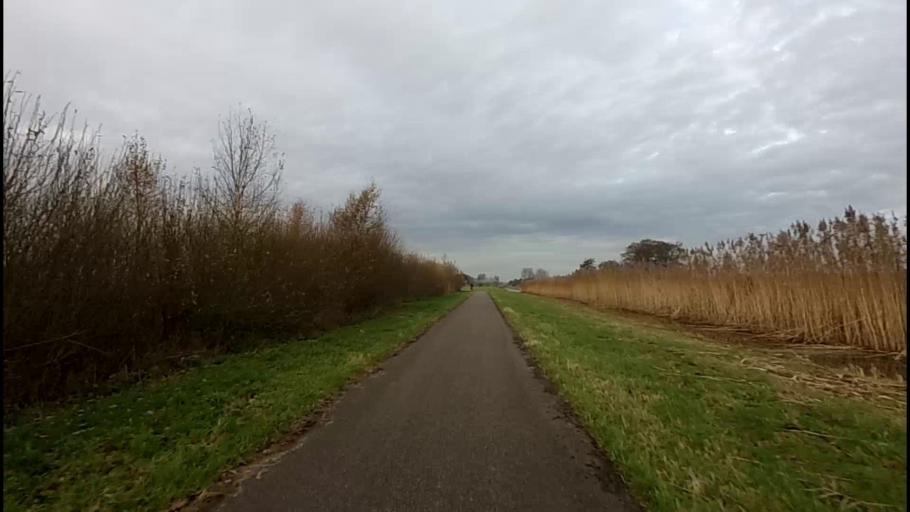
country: NL
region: South Holland
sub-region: Gemeente Vlist
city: Haastrecht
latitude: 51.9472
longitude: 4.7431
